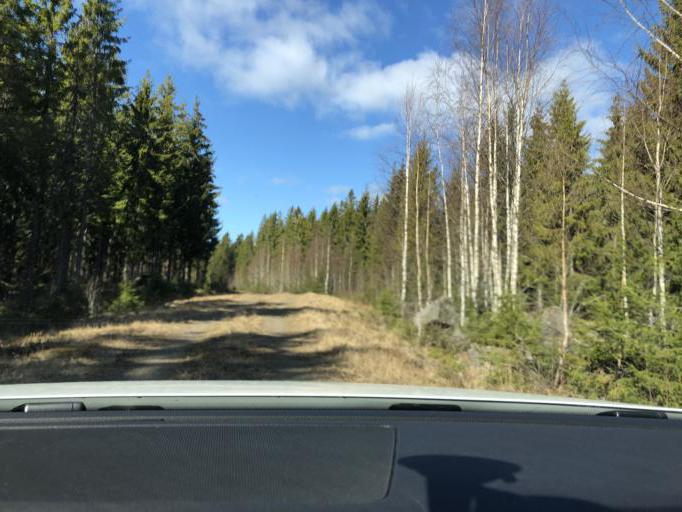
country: SE
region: Uppsala
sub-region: Heby Kommun
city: OEstervala
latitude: 60.2648
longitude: 17.1442
